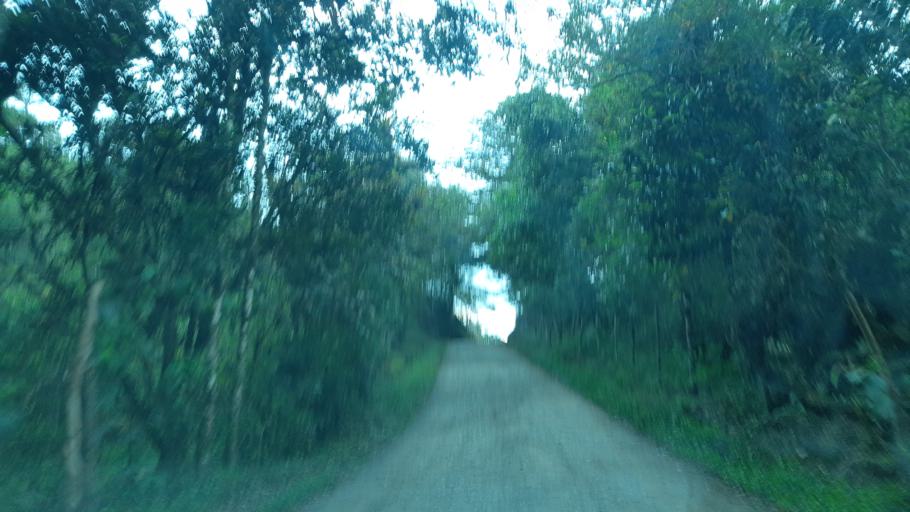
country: CO
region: Boyaca
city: Garagoa
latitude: 5.1075
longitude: -73.3565
